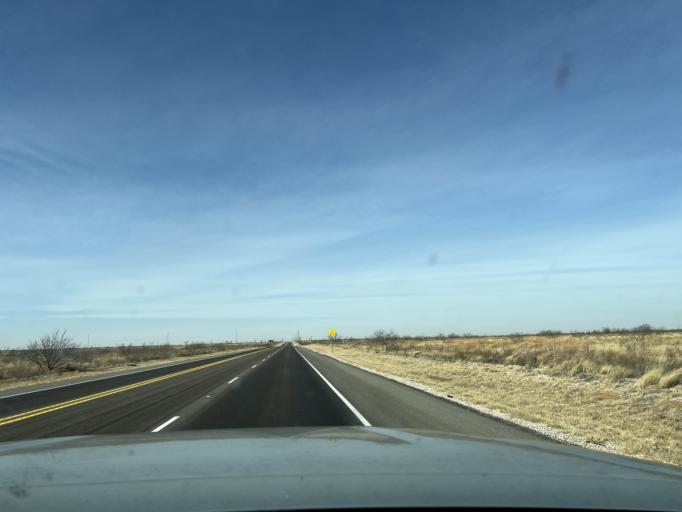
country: US
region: Texas
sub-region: Andrews County
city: Andrews
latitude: 32.3309
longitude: -102.6442
